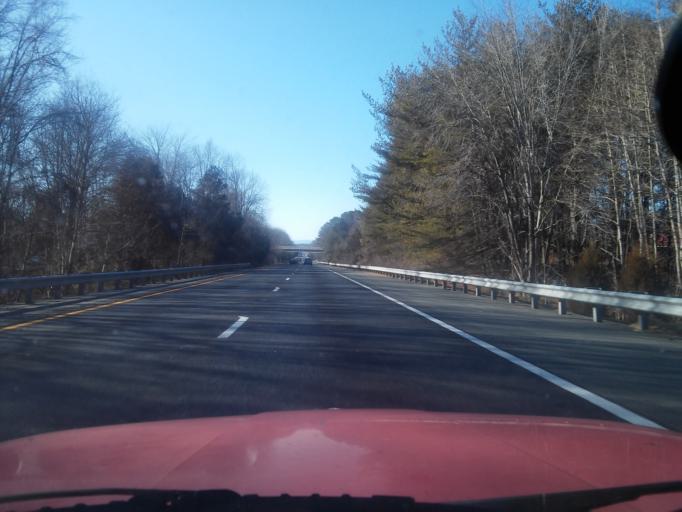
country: US
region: Virginia
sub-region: City of Charlottesville
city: Charlottesville
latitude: 38.0120
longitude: -78.3794
